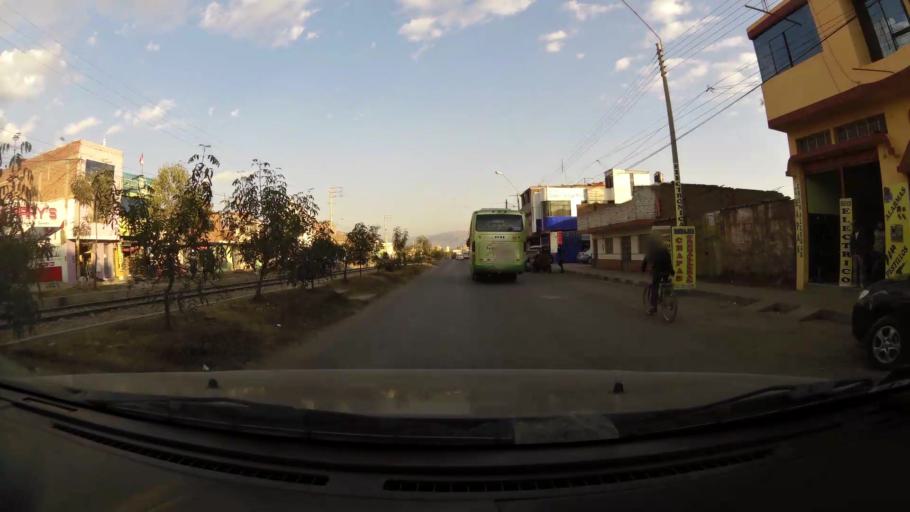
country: PE
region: Junin
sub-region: Provincia de Huancayo
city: El Tambo
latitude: -12.0504
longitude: -75.2152
